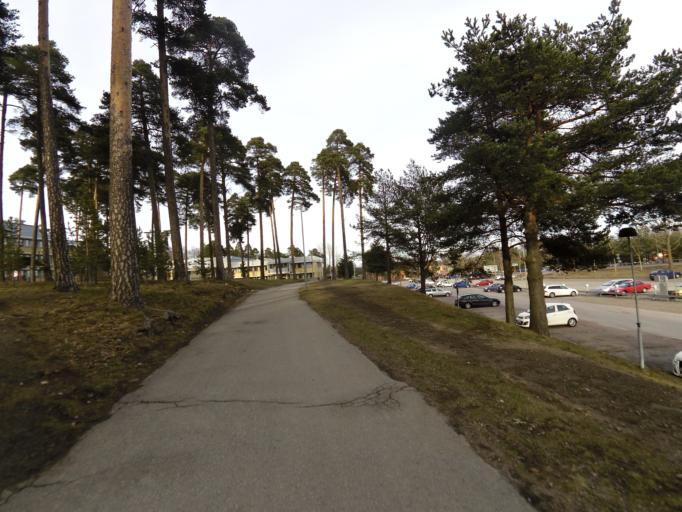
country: SE
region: Gaevleborg
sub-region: Gavle Kommun
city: Gavle
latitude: 60.6788
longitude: 17.1208
